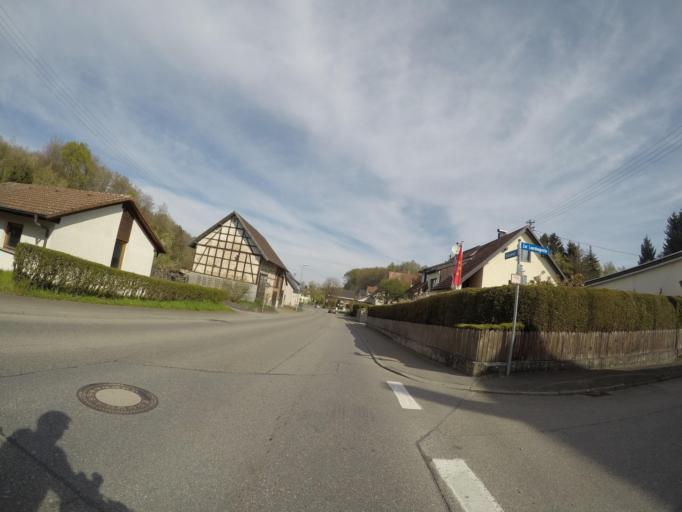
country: DE
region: Baden-Wuerttemberg
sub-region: Tuebingen Region
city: Allmannsweiler
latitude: 48.0065
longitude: 9.5639
